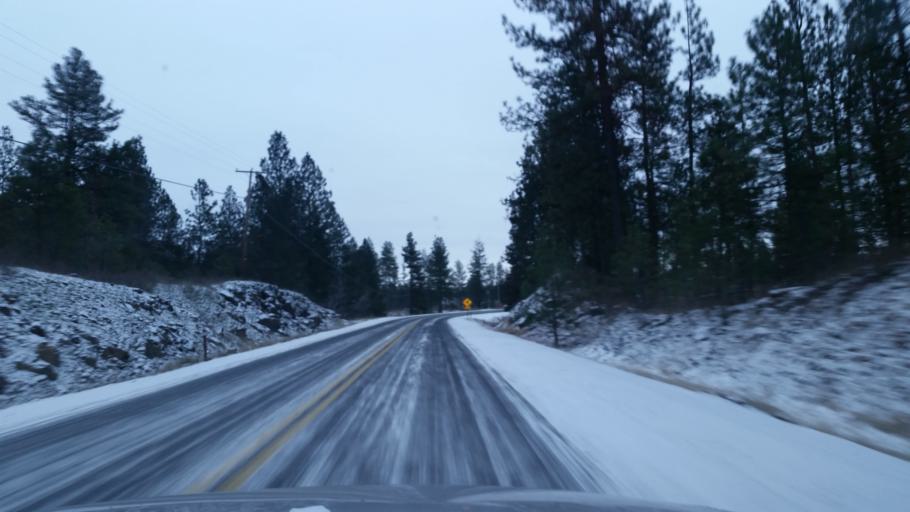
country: US
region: Washington
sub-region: Spokane County
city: Cheney
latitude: 47.4742
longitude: -117.5477
